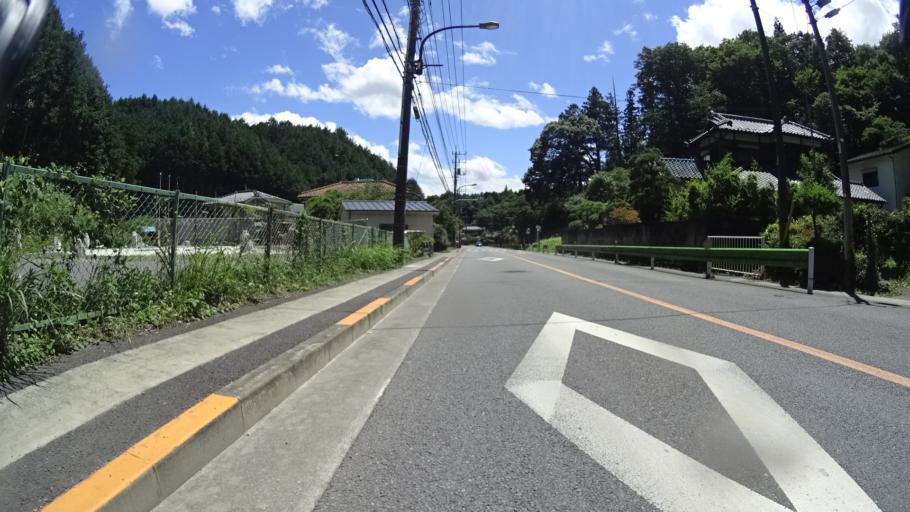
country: JP
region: Tokyo
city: Ome
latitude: 35.8013
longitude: 139.2654
